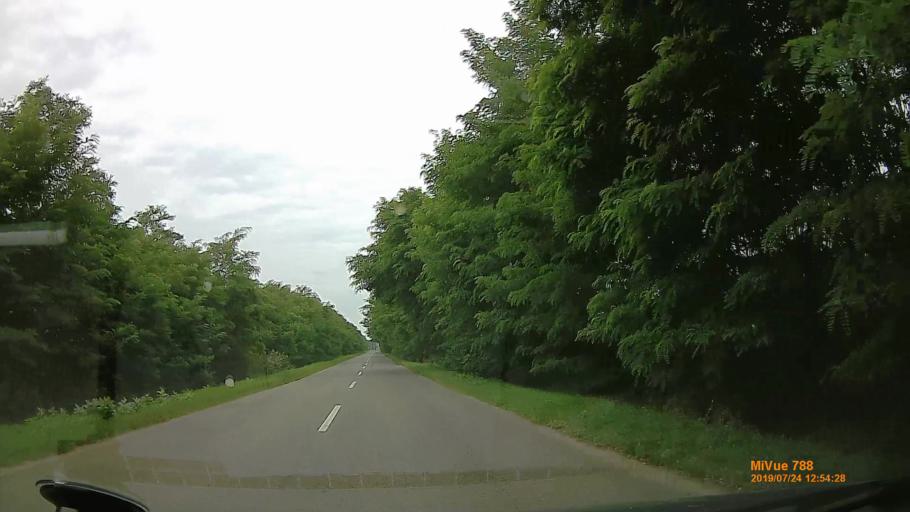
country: HU
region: Szabolcs-Szatmar-Bereg
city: Aranyosapati
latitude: 48.2159
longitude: 22.2987
